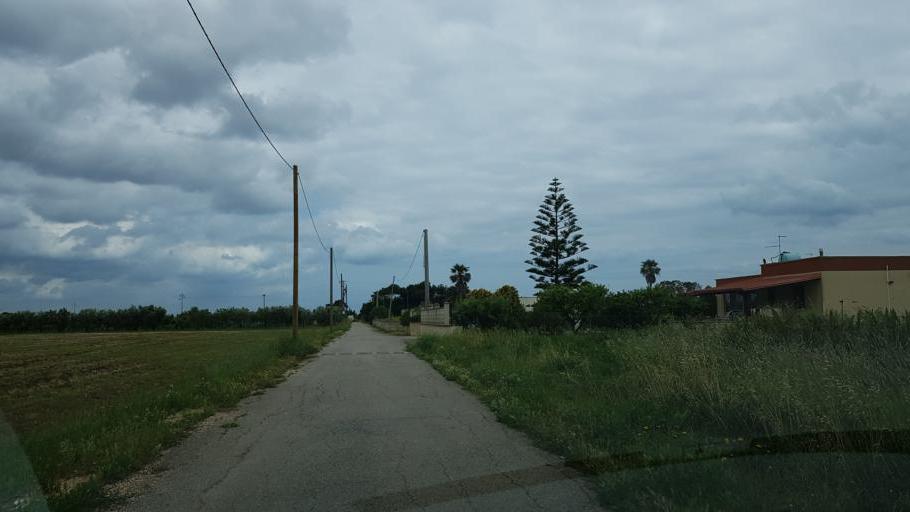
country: IT
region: Apulia
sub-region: Provincia di Brindisi
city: Brindisi
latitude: 40.6345
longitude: 17.8765
